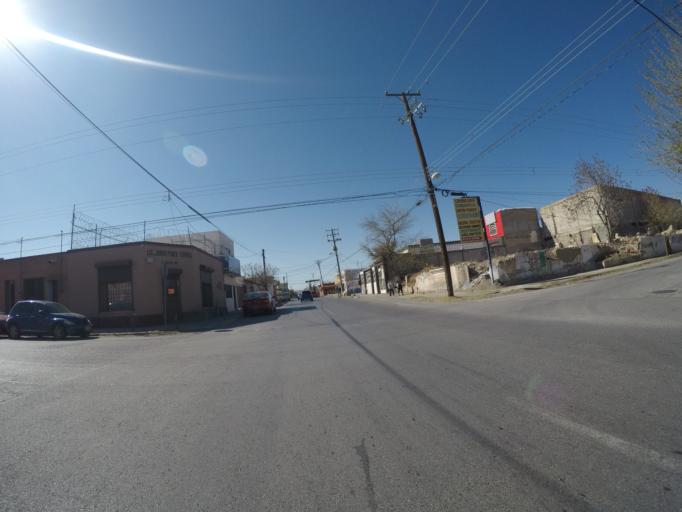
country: MX
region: Chihuahua
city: Ciudad Juarez
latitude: 31.7343
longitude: -106.4743
